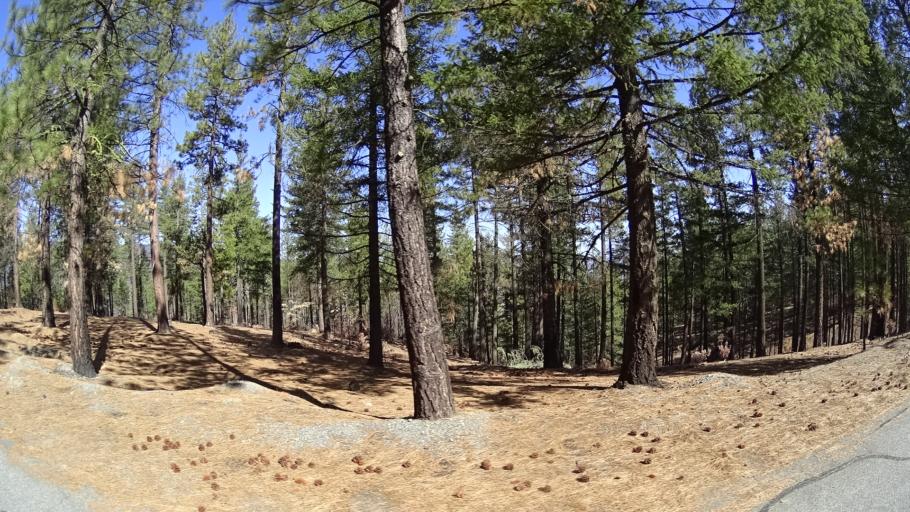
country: US
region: California
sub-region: Tehama County
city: Rancho Tehama Reserve
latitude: 39.6513
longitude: -122.7305
